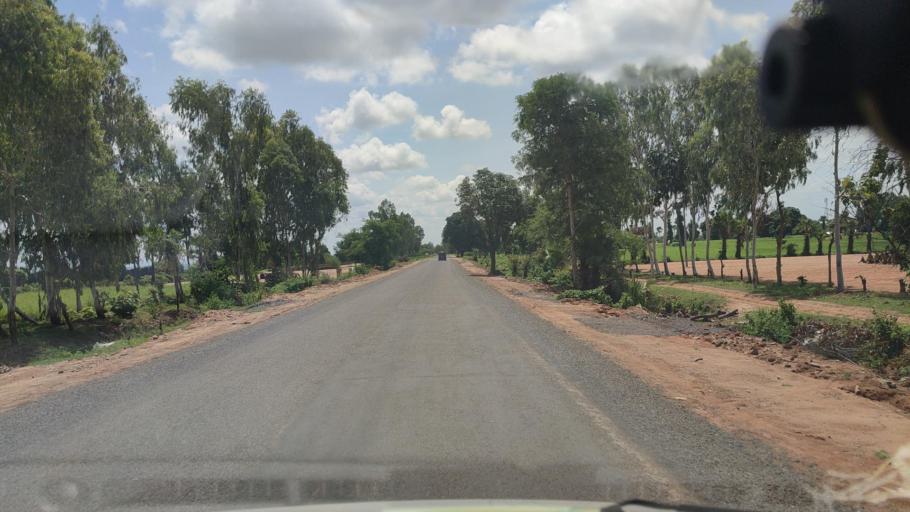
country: MM
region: Magway
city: Magway
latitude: 20.1941
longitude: 95.0820
